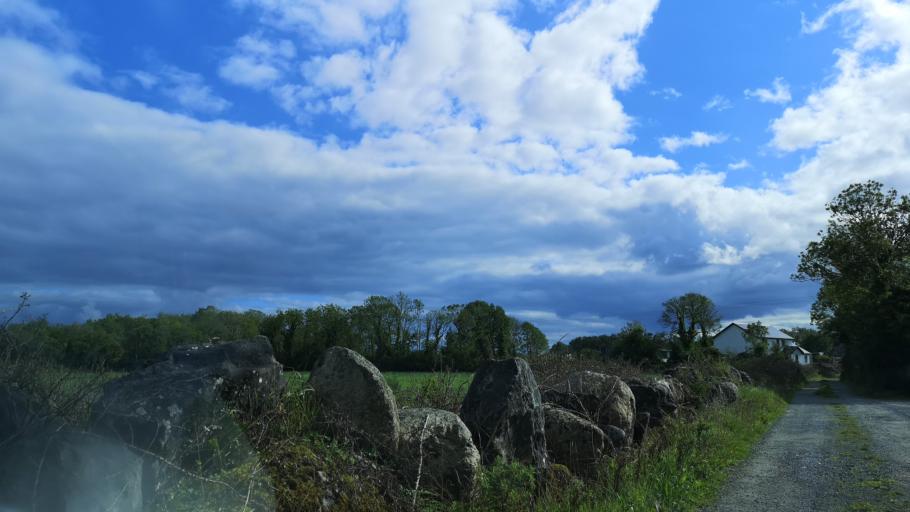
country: IE
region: Connaught
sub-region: County Galway
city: Moycullen
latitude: 53.3552
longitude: -9.1577
